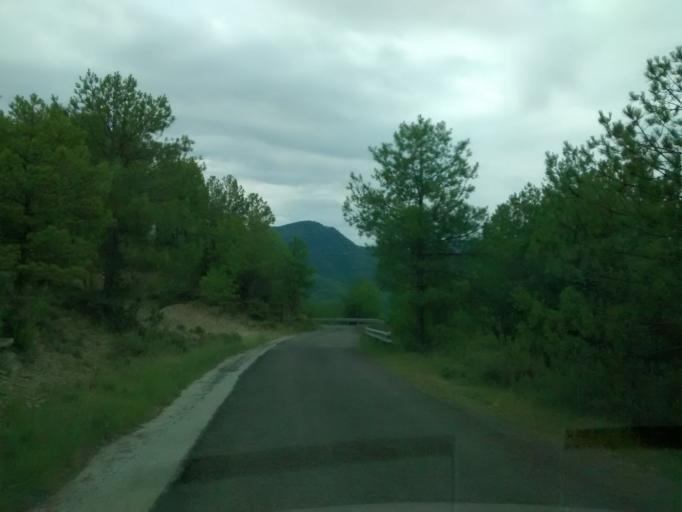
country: ES
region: Aragon
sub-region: Provincia de Huesca
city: Laspuna
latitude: 42.5182
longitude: 0.1310
